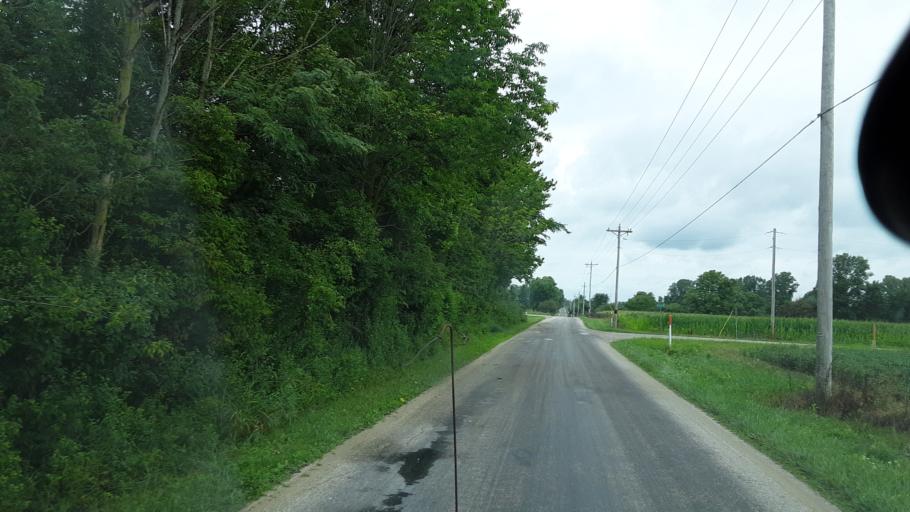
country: US
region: Indiana
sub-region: Adams County
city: Geneva
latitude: 40.5202
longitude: -85.0100
